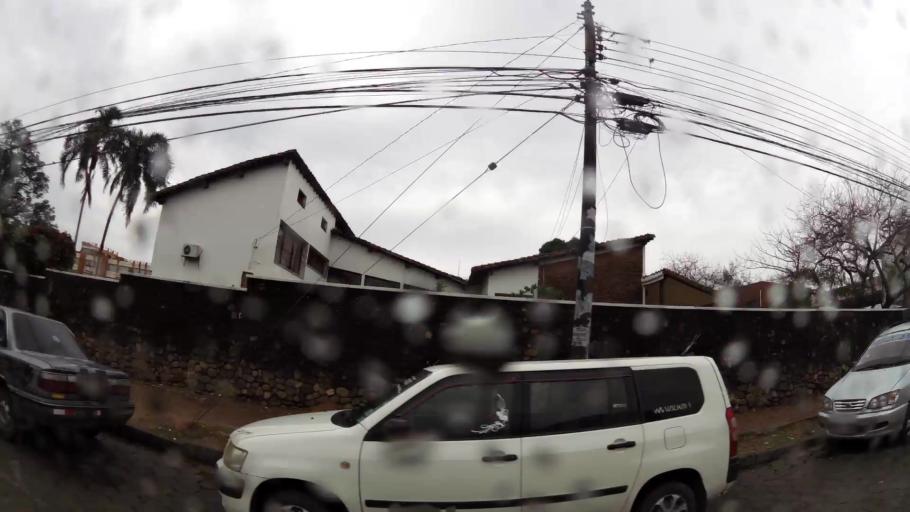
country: BO
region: Santa Cruz
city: Santa Cruz de la Sierra
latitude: -17.7920
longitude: -63.1857
